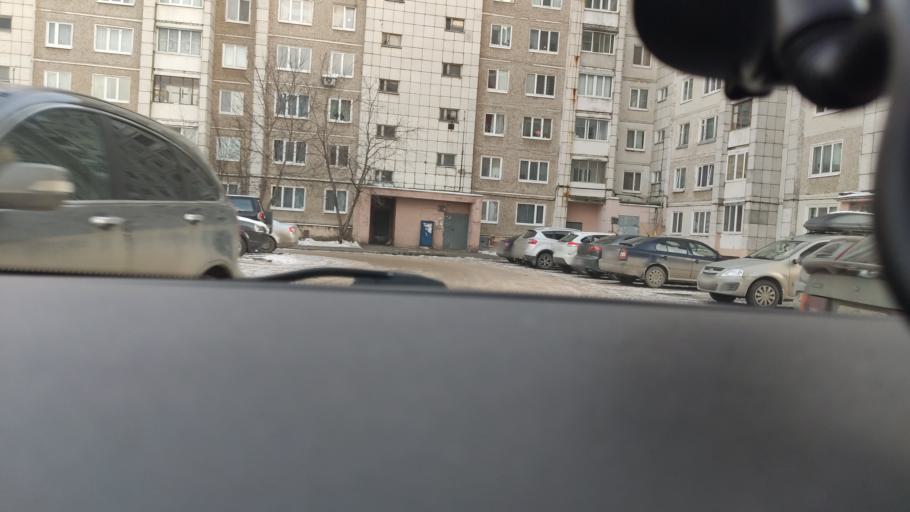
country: RU
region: Perm
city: Perm
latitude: 58.1100
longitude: 56.2883
